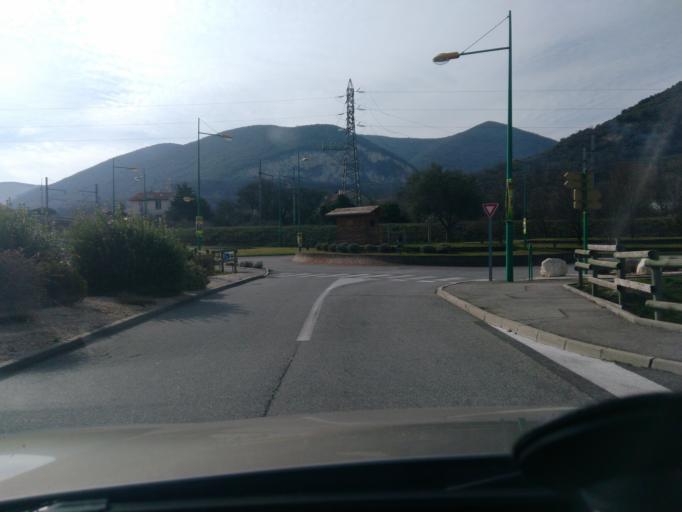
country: FR
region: Rhone-Alpes
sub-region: Departement de l'Ardeche
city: Cruas
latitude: 44.6588
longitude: 4.7676
